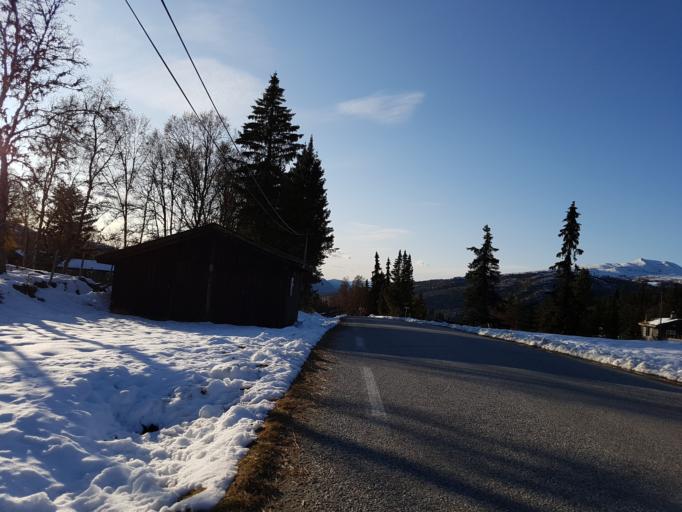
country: NO
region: Oppland
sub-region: Sel
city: Otta
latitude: 61.8093
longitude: 9.6791
